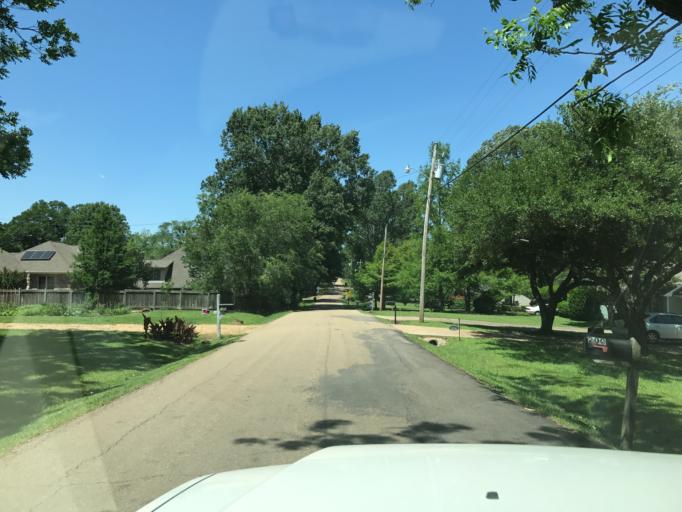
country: US
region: Mississippi
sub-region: Madison County
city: Ridgeland
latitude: 32.4324
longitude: -90.1335
